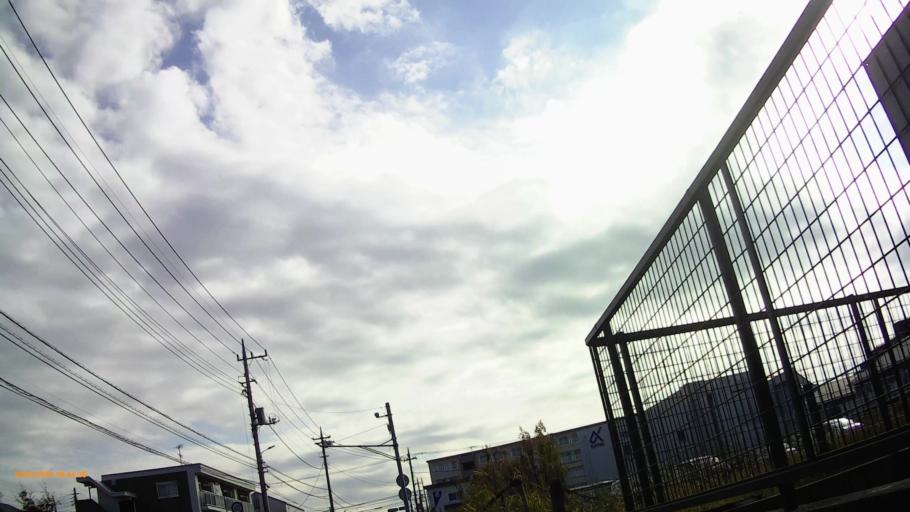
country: JP
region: Chiba
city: Yotsukaido
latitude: 35.6257
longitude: 140.1939
